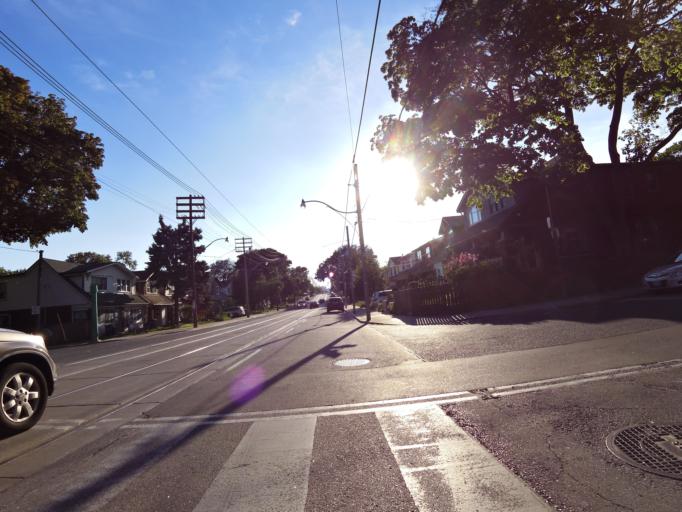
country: CA
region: Ontario
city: Toronto
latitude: 43.6704
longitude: -79.3304
